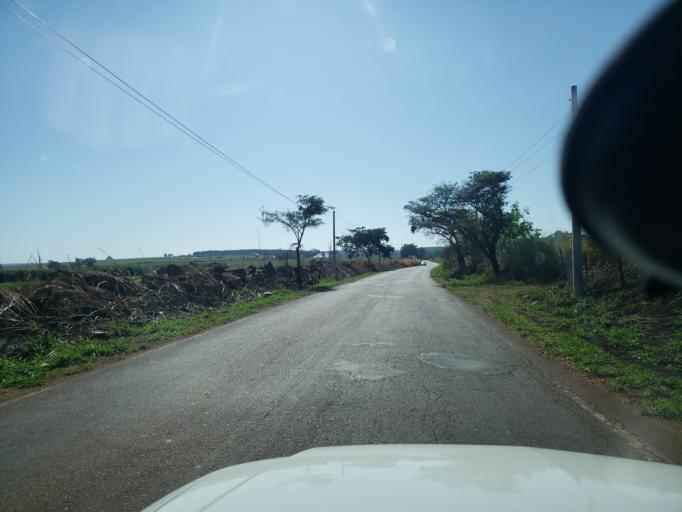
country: BR
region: Sao Paulo
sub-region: Moji-Guacu
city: Mogi-Gaucu
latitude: -22.3398
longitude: -46.8868
